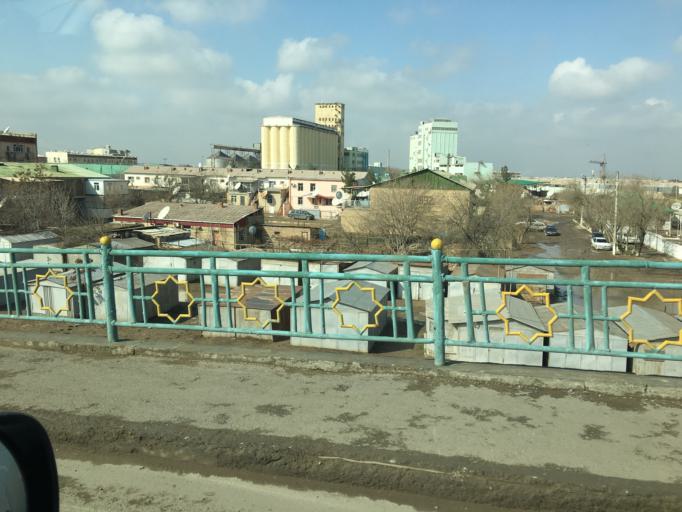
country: TM
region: Mary
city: Mary
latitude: 37.5990
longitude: 61.8308
